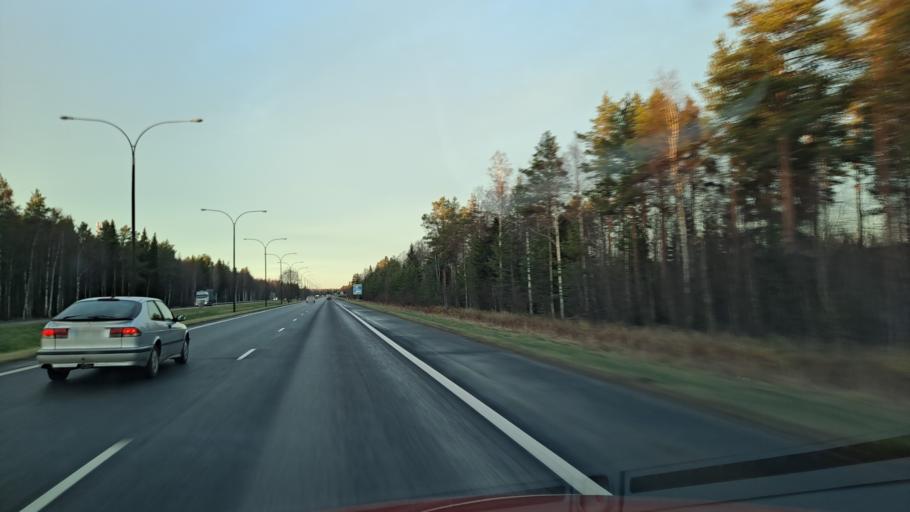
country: FI
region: Northern Ostrobothnia
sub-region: Oulu
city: Oulu
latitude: 65.0899
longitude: 25.4378
